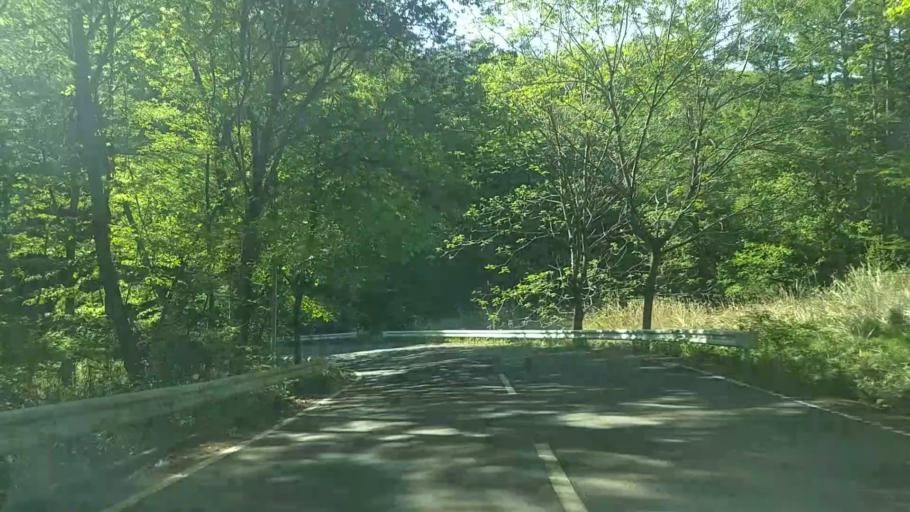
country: JP
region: Yamanashi
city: Nirasaki
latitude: 35.8839
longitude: 138.3762
